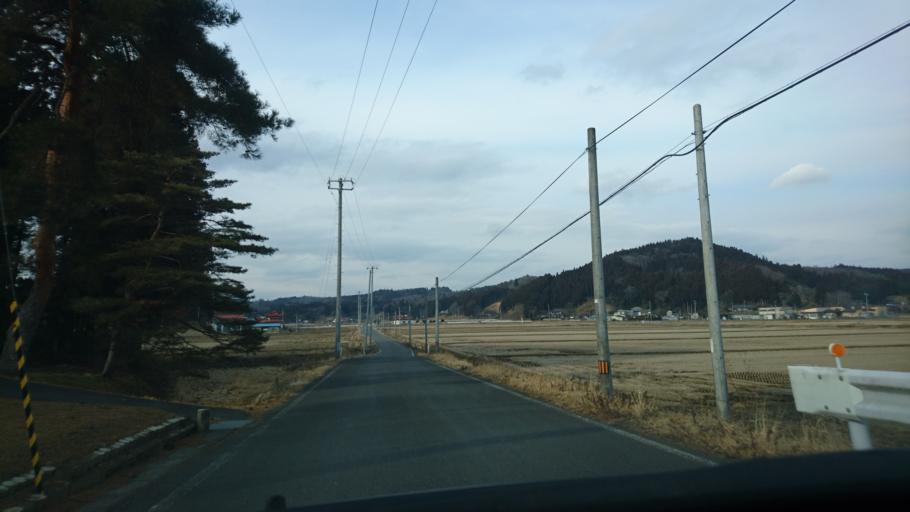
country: JP
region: Iwate
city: Ichinoseki
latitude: 38.8299
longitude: 141.2476
